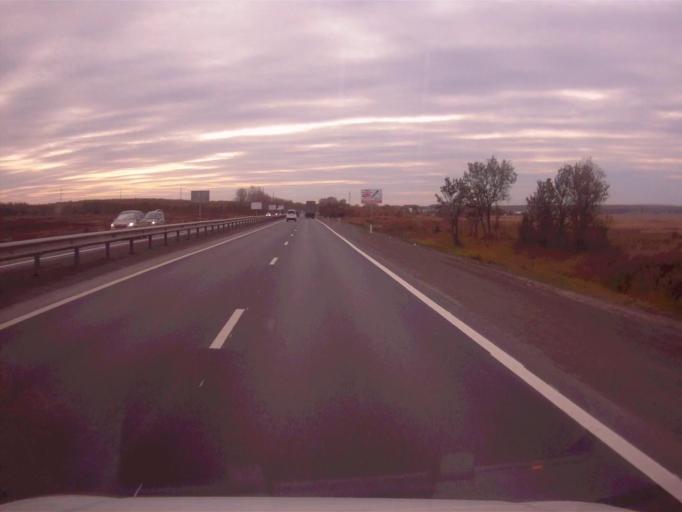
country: RU
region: Chelyabinsk
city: Roza
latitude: 54.9894
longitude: 61.4399
